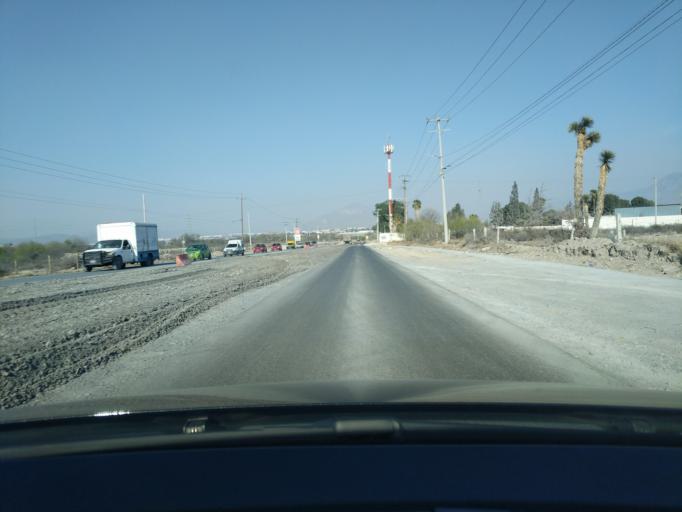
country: MX
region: Coahuila
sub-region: Ramos Arizpe
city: Ramos Arizpe
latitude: 25.5362
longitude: -100.9710
